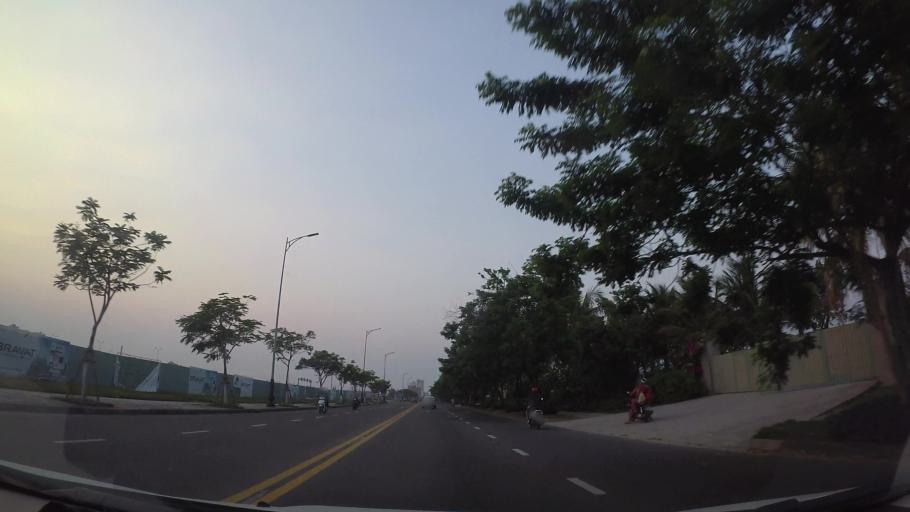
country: VN
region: Da Nang
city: Ngu Hanh Son
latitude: 16.0174
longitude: 108.2600
